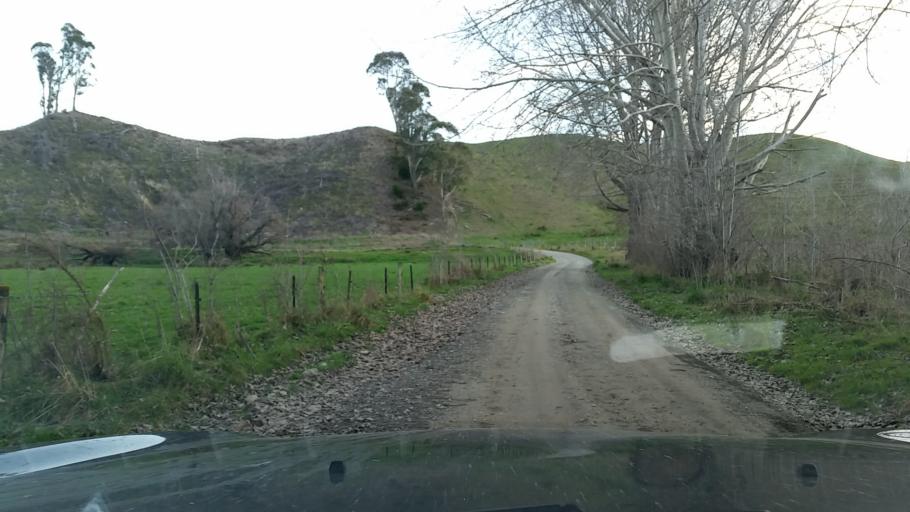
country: NZ
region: Marlborough
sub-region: Marlborough District
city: Blenheim
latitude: -41.5083
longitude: 173.5914
